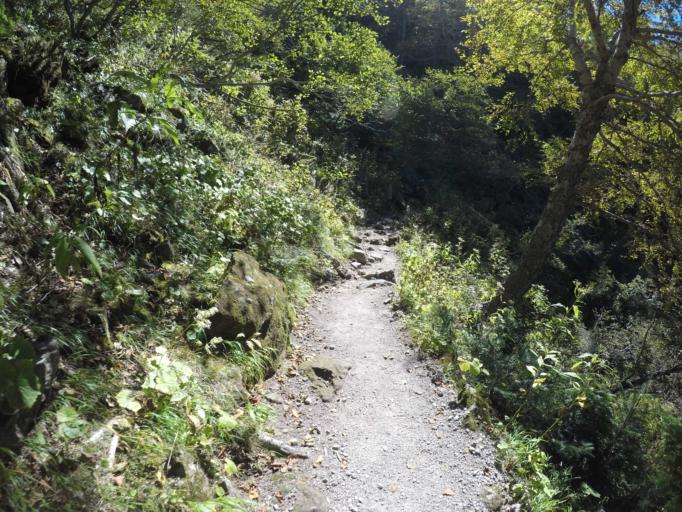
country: JP
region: Tochigi
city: Nikko
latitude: 36.8007
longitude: 139.3683
